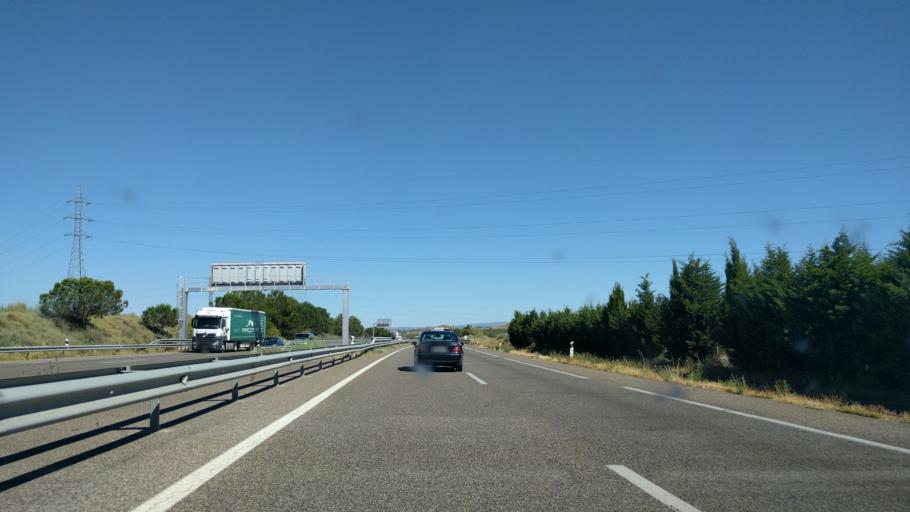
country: ES
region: Catalonia
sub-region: Provincia de Lleida
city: Alcoletge
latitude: 41.6345
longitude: 0.6903
